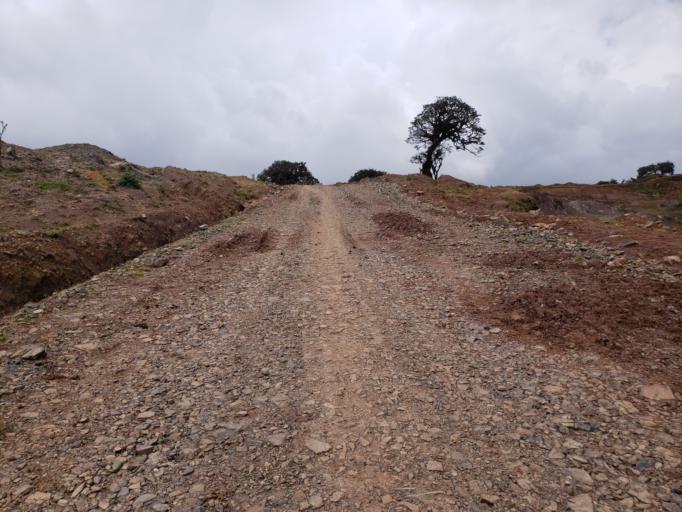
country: ET
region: Oromiya
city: Dodola
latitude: 6.6507
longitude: 39.3635
